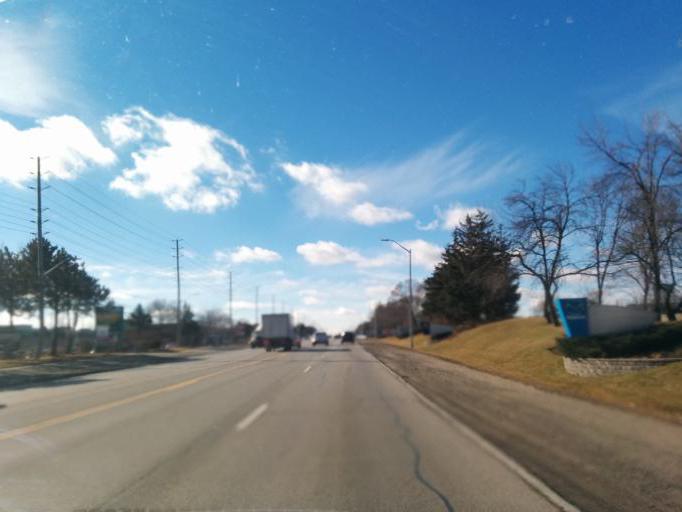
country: CA
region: Ontario
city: Mississauga
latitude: 43.5295
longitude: -79.6743
